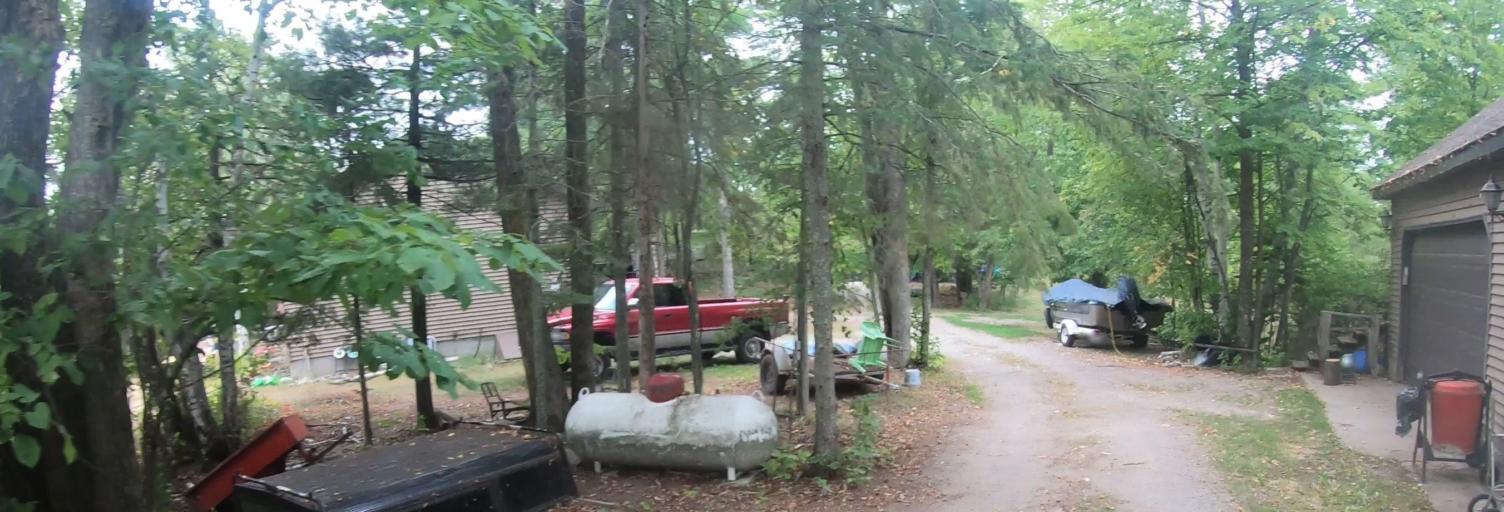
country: US
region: Minnesota
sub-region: Saint Louis County
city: Mountain Iron
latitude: 47.9403
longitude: -92.6250
